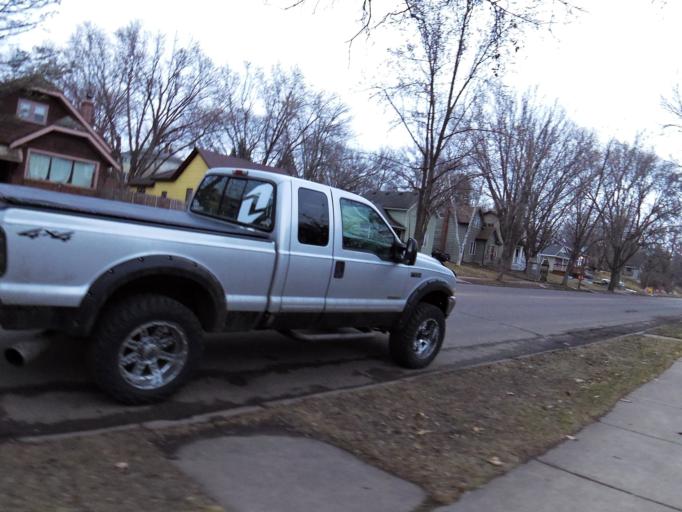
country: US
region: Wisconsin
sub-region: Saint Croix County
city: Hudson
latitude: 44.9821
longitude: -92.7573
